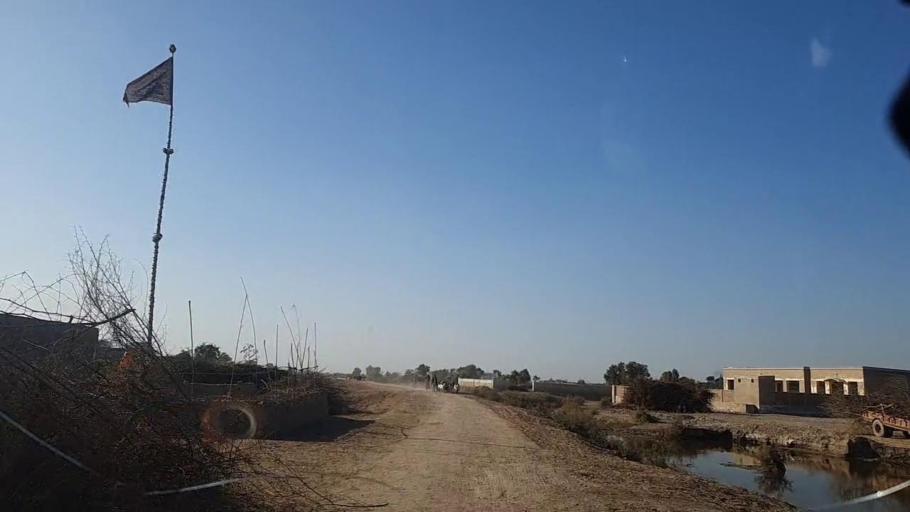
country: PK
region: Sindh
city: Khanpur
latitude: 27.7690
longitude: 69.2937
